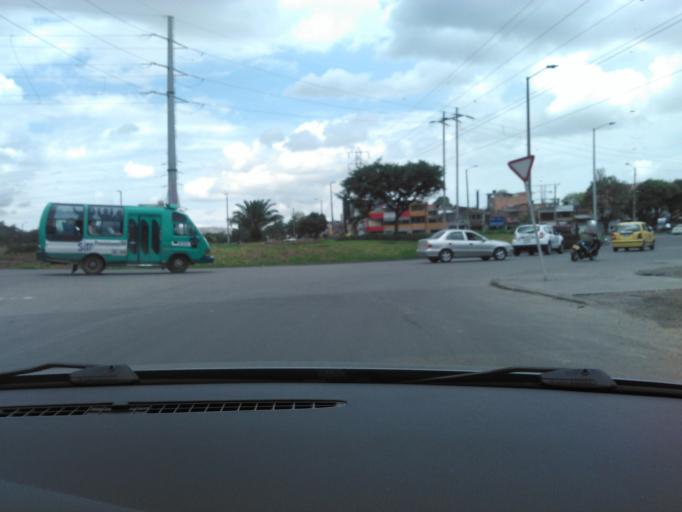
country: CO
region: Bogota D.C.
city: Bogota
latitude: 4.6154
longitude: -74.1140
